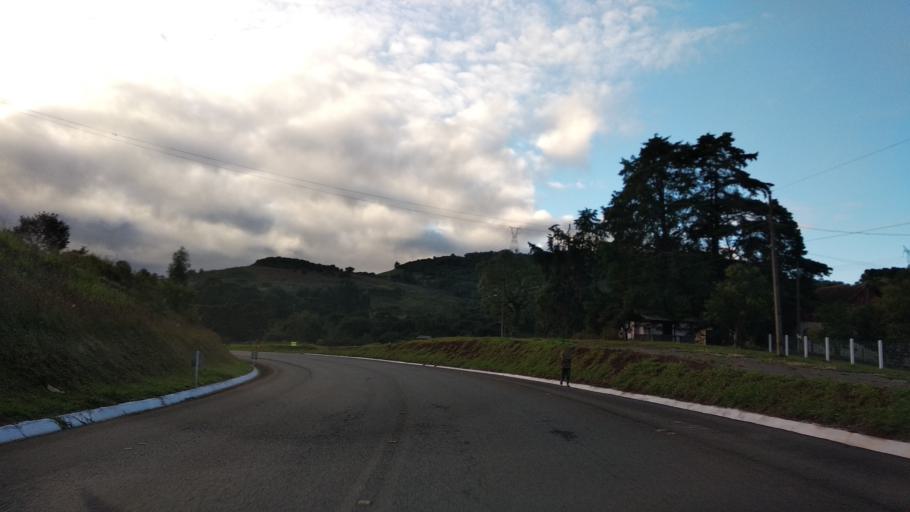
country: BR
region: Santa Catarina
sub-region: Curitibanos
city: Curitibanos
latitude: -27.5610
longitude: -50.8393
